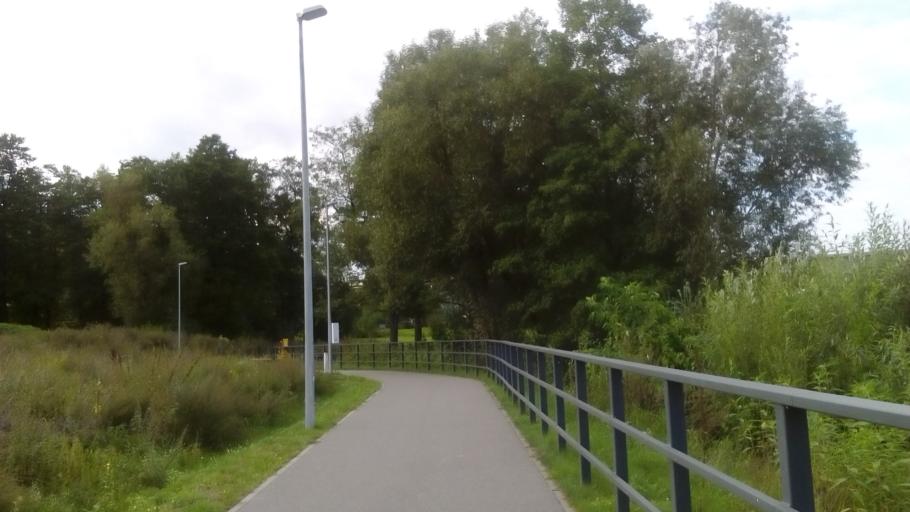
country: LT
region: Alytaus apskritis
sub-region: Alytus
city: Alytus
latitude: 54.4187
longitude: 24.0405
